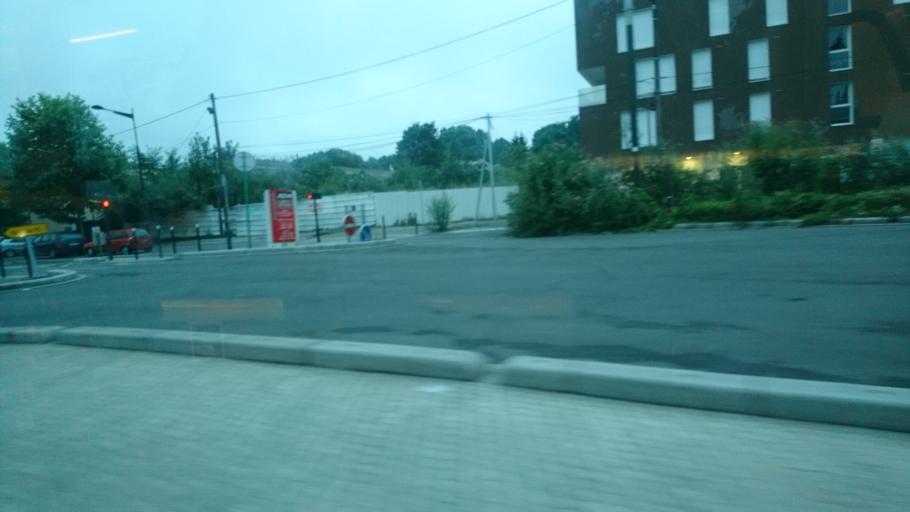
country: FR
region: Ile-de-France
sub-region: Departement de Seine-Saint-Denis
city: Pierrefitte-sur-Seine
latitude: 48.9741
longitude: 2.3659
